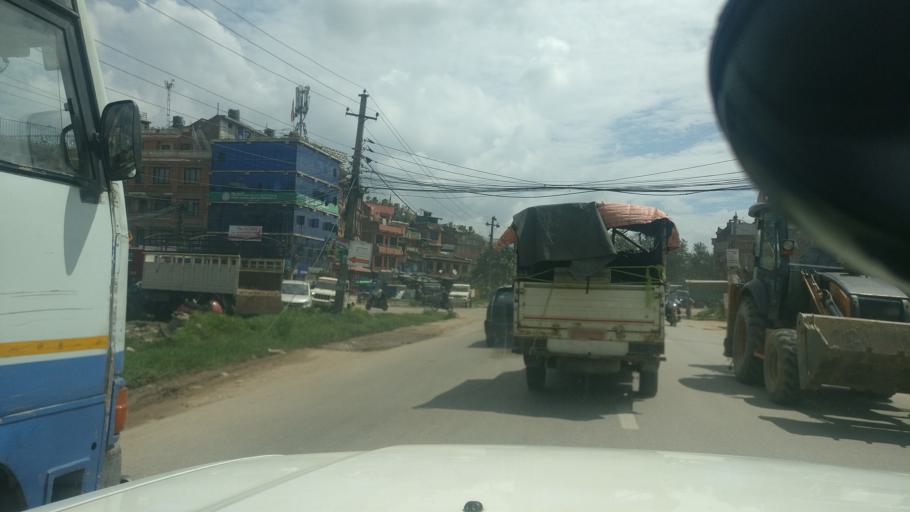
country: NP
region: Central Region
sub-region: Bagmati Zone
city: Bhaktapur
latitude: 27.6665
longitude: 85.4360
